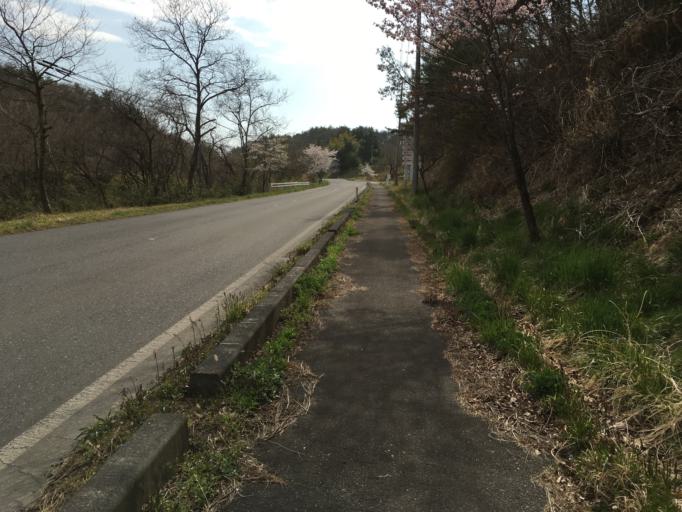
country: JP
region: Iwate
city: Ichinoseki
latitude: 38.8142
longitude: 141.1449
